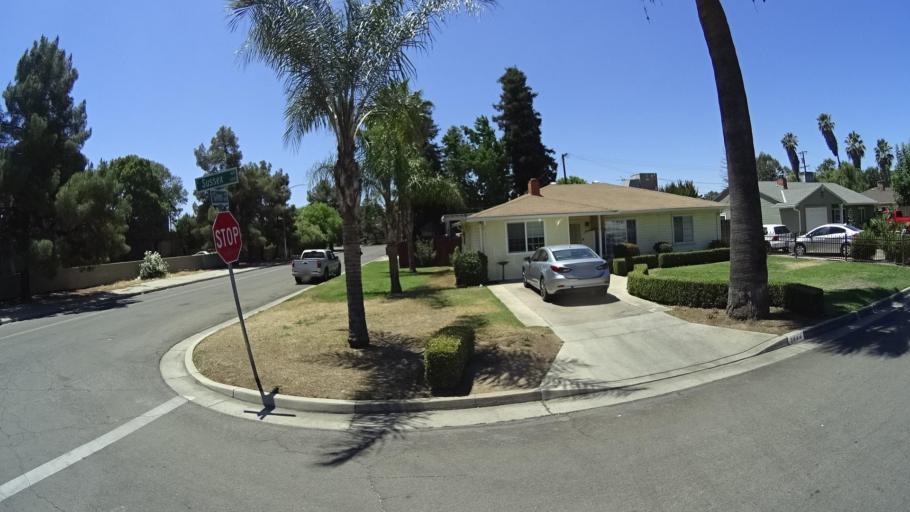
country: US
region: California
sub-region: Fresno County
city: Fresno
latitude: 36.7914
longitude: -119.7930
